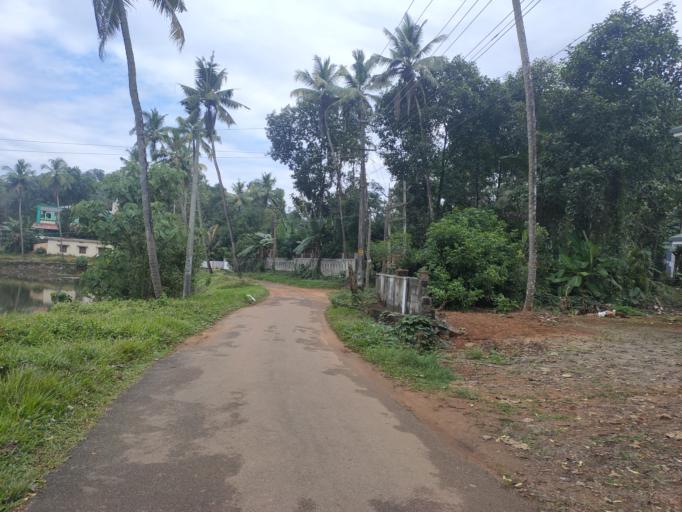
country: IN
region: Kerala
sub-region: Ernakulam
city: Muvattupula
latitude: 9.9994
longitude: 76.6372
